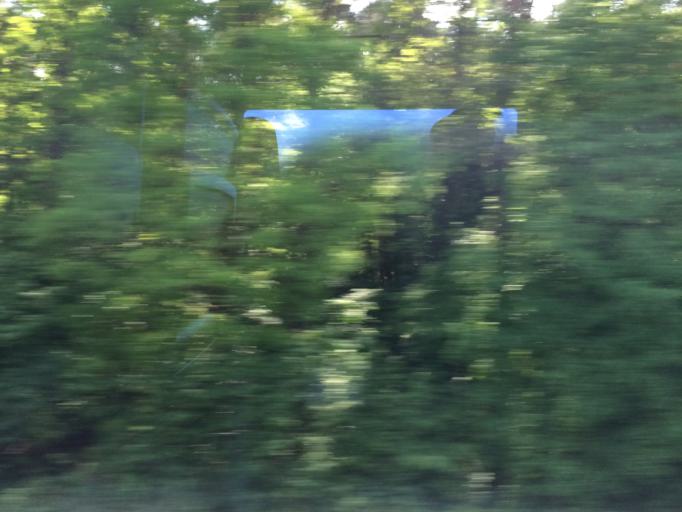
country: DE
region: Bavaria
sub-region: Regierungsbezirk Mittelfranken
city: Langenfeld
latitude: 49.6334
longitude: 10.4849
